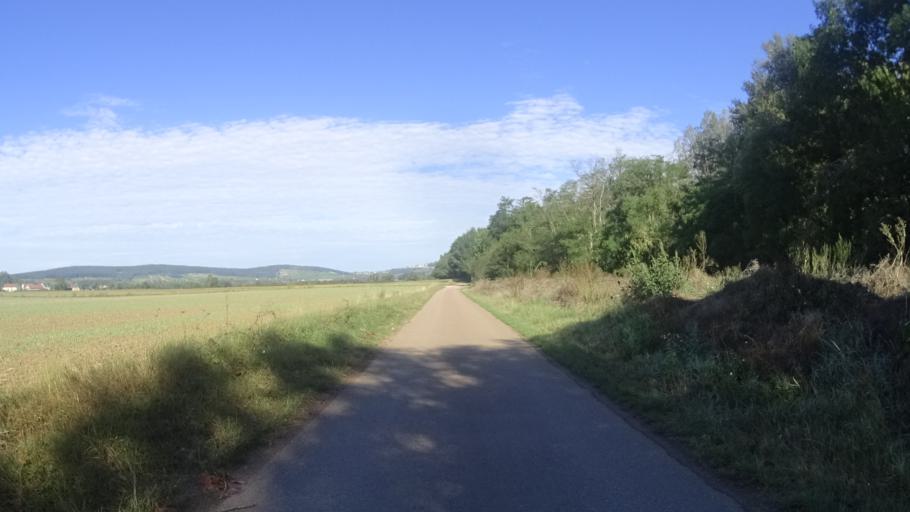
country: FR
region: Bourgogne
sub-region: Departement de la Nievre
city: Pouilly-sur-Loire
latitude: 47.3054
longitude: 2.9009
